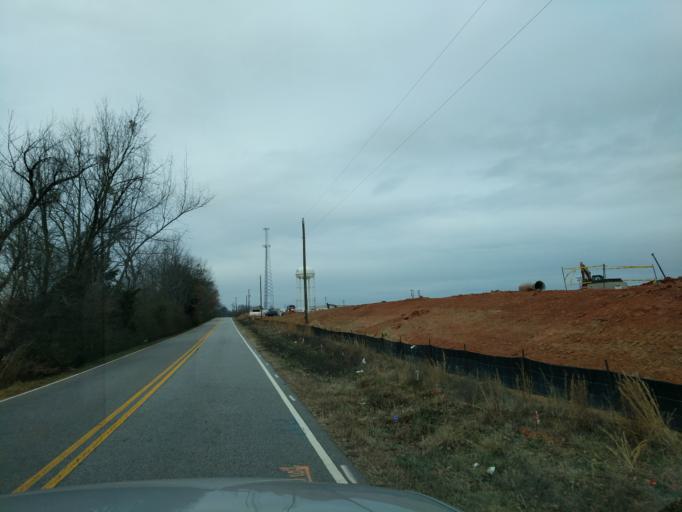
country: US
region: South Carolina
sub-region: Spartanburg County
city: Duncan
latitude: 34.8789
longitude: -82.1417
